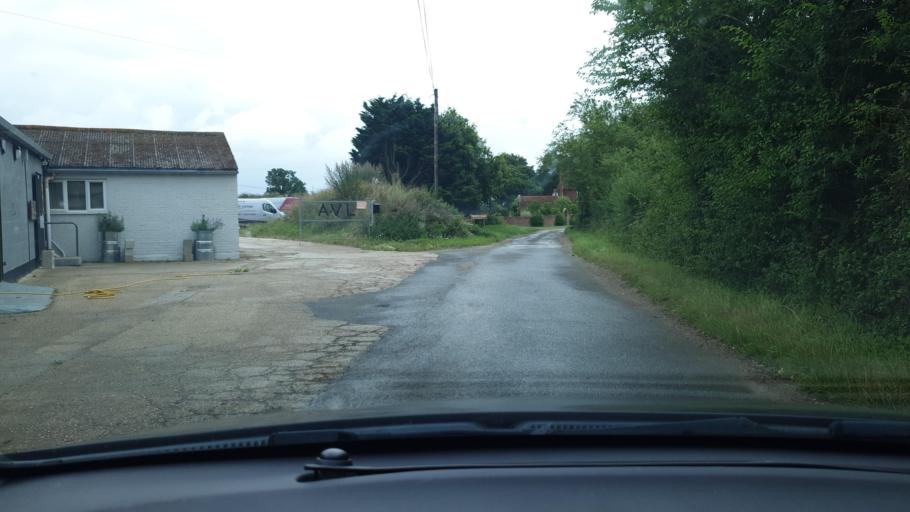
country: GB
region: England
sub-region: Essex
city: Little Clacton
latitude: 51.8653
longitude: 1.1845
